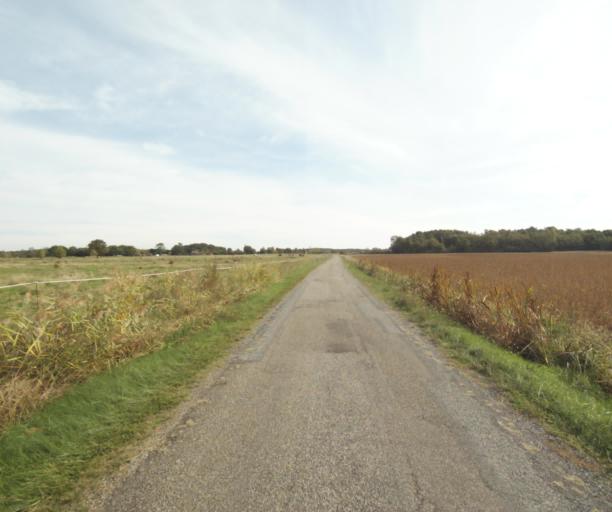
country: FR
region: Midi-Pyrenees
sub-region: Departement du Tarn-et-Garonne
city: Orgueil
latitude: 43.8993
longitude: 1.3866
